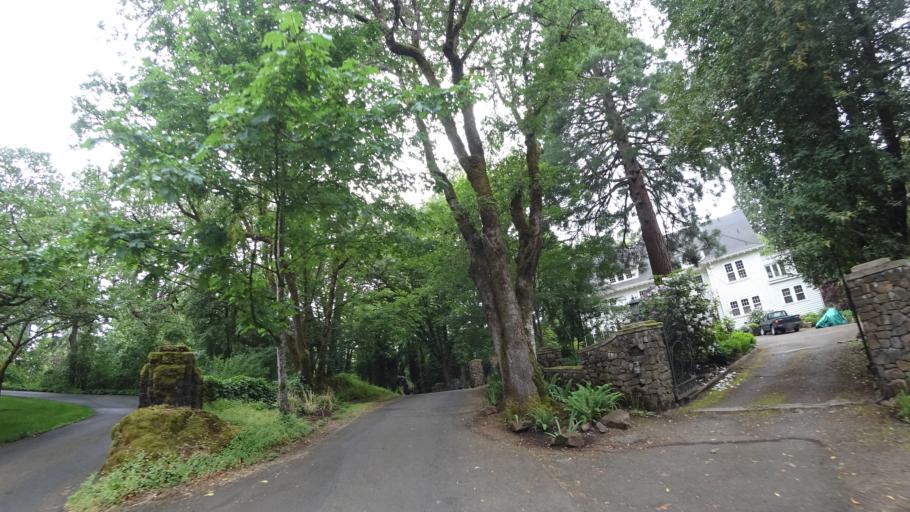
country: US
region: Oregon
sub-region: Clackamas County
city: Milwaukie
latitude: 45.4495
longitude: -122.6482
